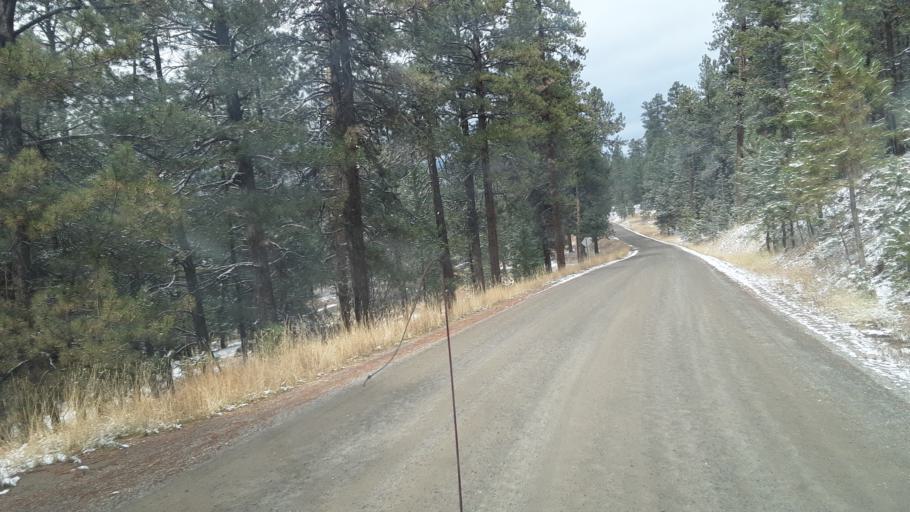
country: US
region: Colorado
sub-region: La Plata County
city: Bayfield
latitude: 37.4073
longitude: -107.5343
